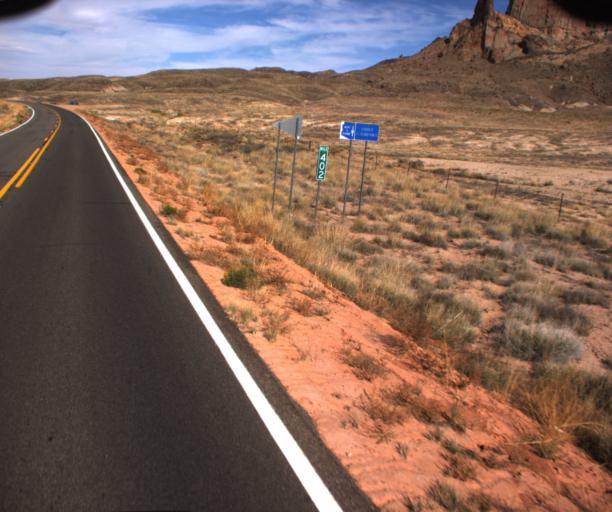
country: US
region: Arizona
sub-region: Navajo County
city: Kayenta
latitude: 36.8170
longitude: -110.2343
